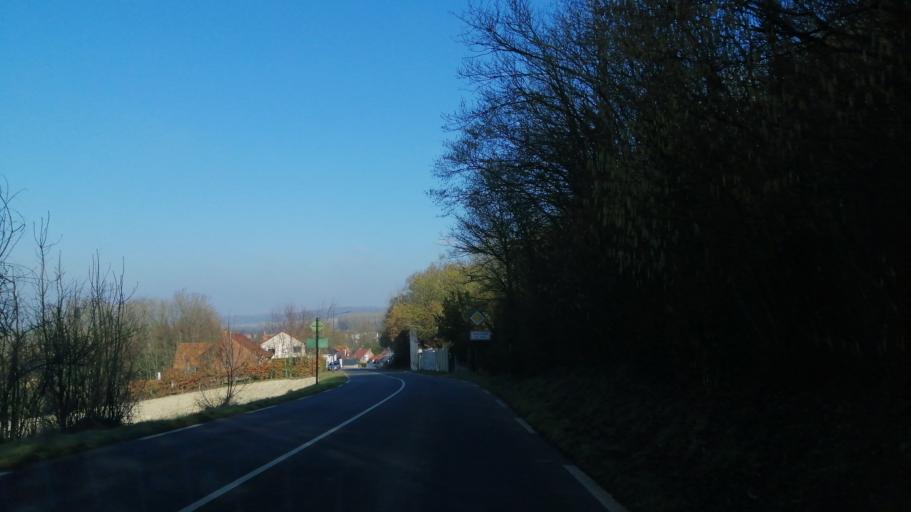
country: FR
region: Nord-Pas-de-Calais
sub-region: Departement du Pas-de-Calais
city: Ranchicourt
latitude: 50.4102
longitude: 2.5866
